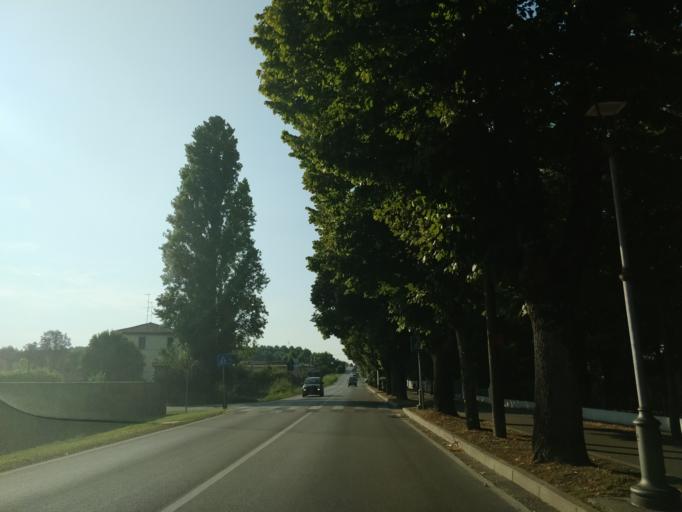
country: IT
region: Emilia-Romagna
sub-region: Provincia di Bologna
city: Pieve di Cento
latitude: 44.7181
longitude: 11.2999
